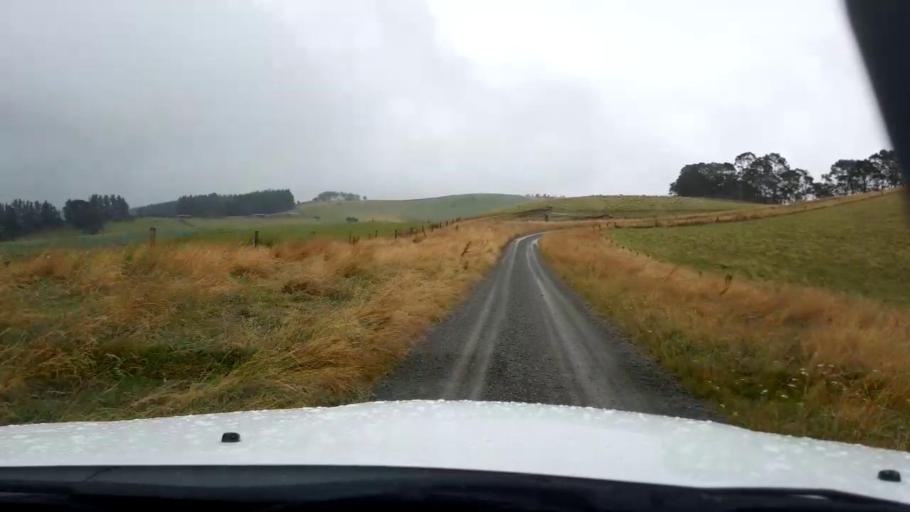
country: NZ
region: Canterbury
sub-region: Timaru District
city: Pleasant Point
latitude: -44.1730
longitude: 171.1068
